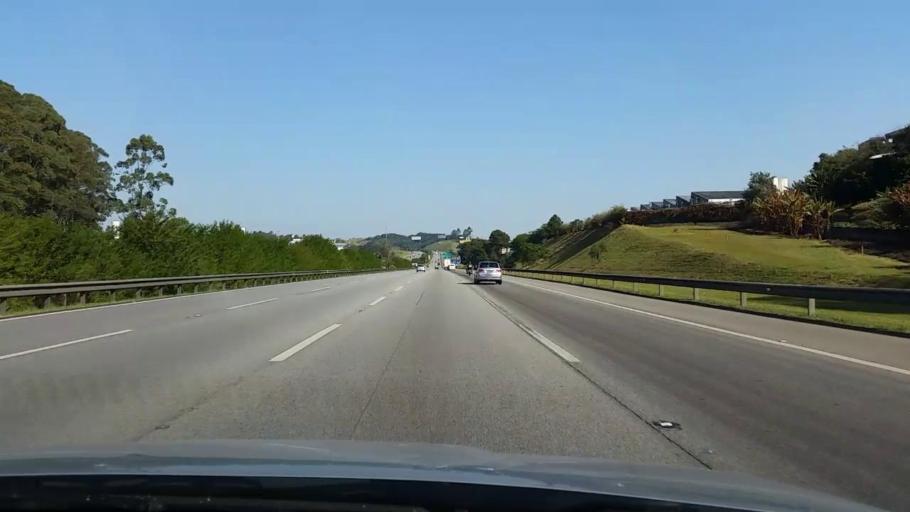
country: BR
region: Sao Paulo
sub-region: Diadema
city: Diadema
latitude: -23.7115
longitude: -46.6043
